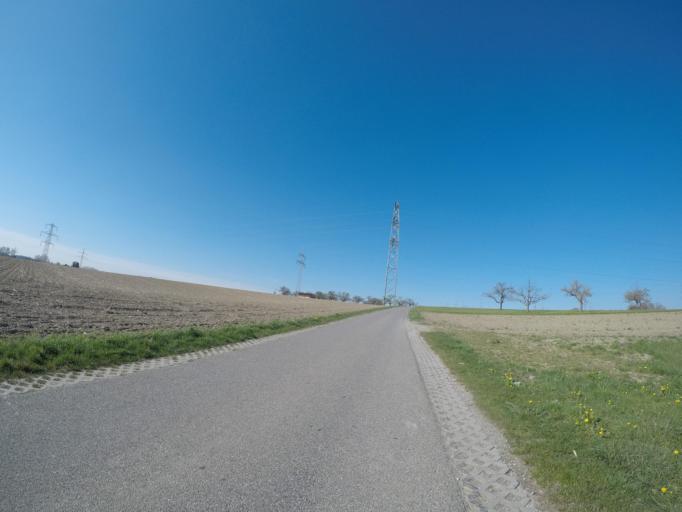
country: DE
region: Baden-Wuerttemberg
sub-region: Tuebingen Region
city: Ebenweiler
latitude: 47.9105
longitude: 9.5181
